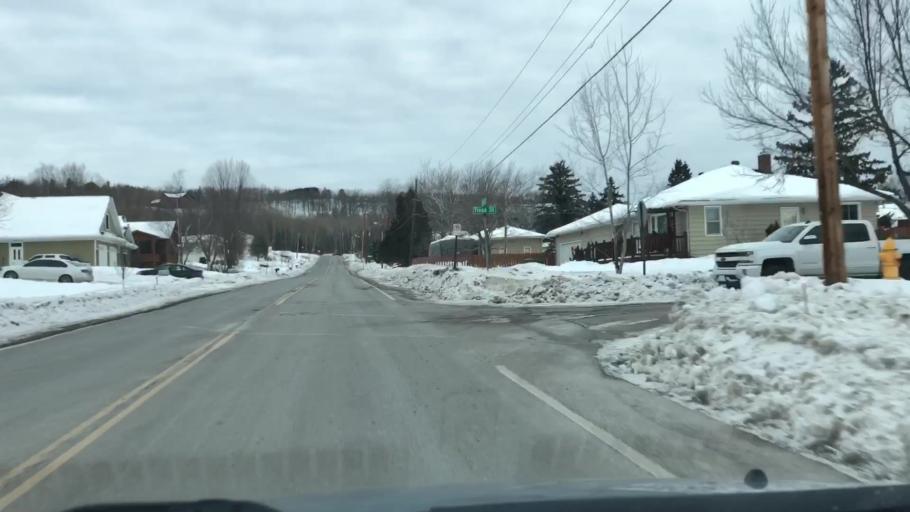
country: US
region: Minnesota
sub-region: Saint Louis County
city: Arnold
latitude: 46.8372
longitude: -92.0371
